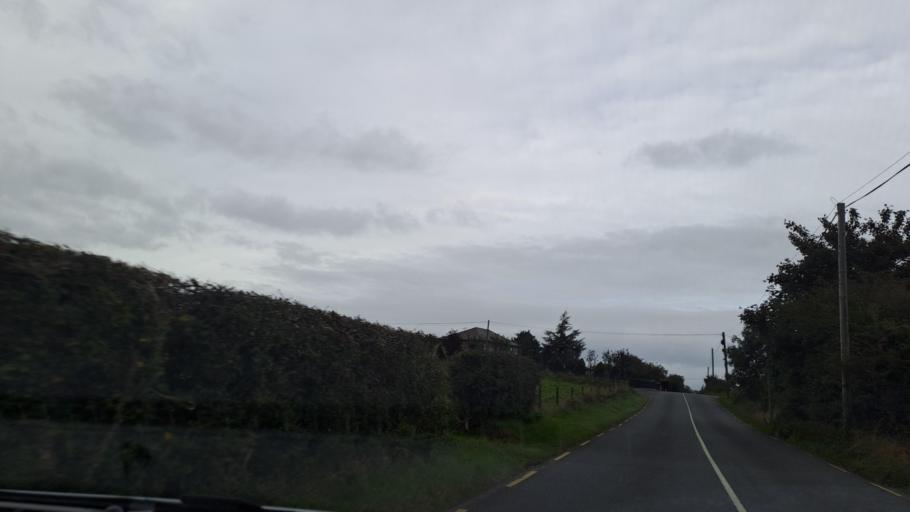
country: IE
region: Ulster
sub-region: An Cabhan
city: Bailieborough
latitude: 54.0187
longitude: -6.9087
